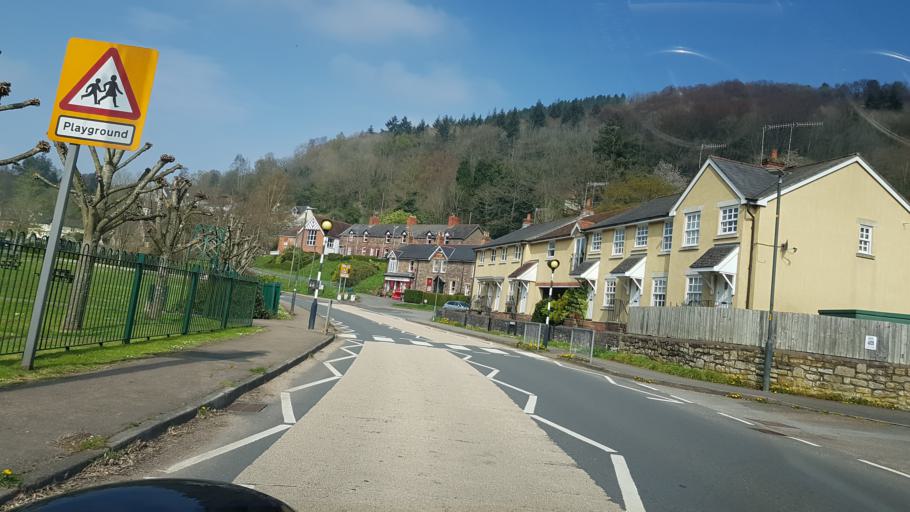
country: GB
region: Wales
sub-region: Monmouthshire
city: Monmouth
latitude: 51.7841
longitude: -2.6727
